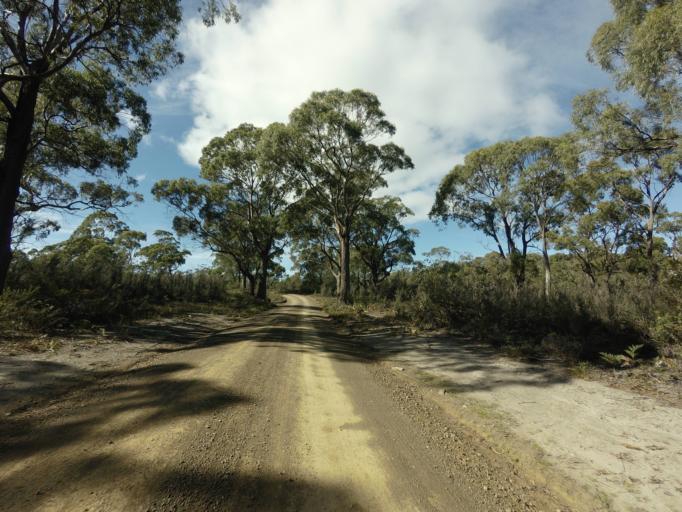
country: AU
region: Tasmania
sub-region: Clarence
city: Sandford
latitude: -42.9659
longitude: 147.7077
